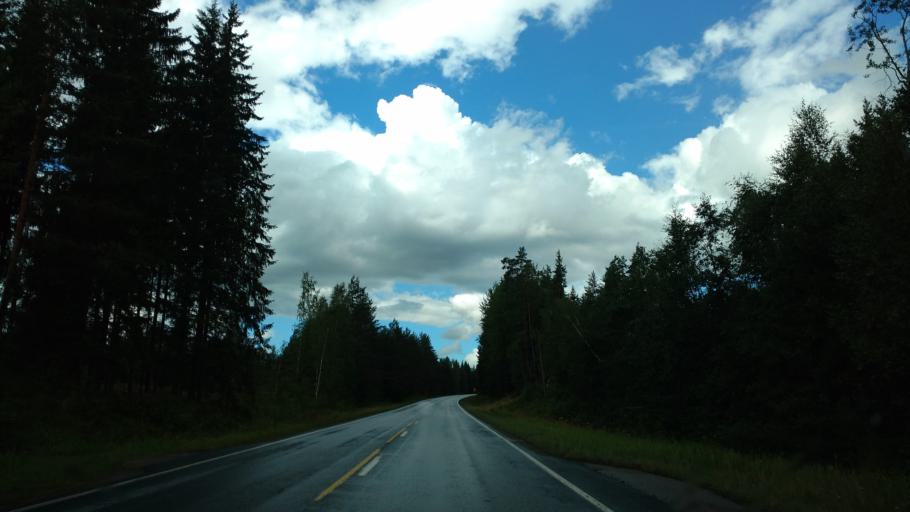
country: FI
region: Varsinais-Suomi
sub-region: Salo
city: Muurla
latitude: 60.2896
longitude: 23.3495
